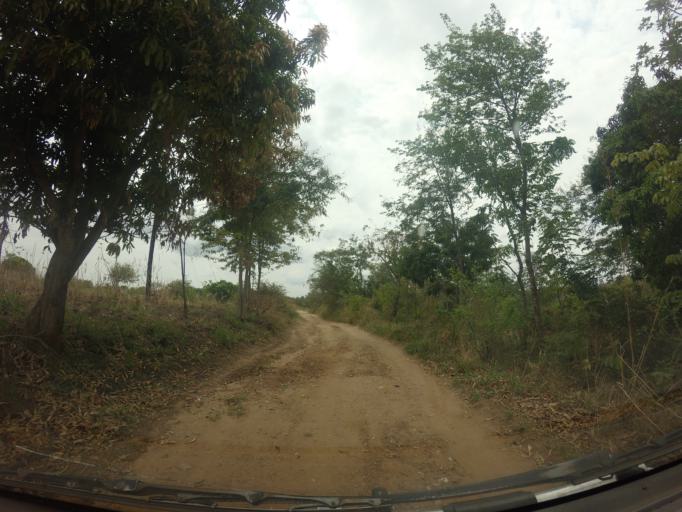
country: UG
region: Northern Region
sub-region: Arua District
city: Arua
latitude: 2.9403
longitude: 30.9395
